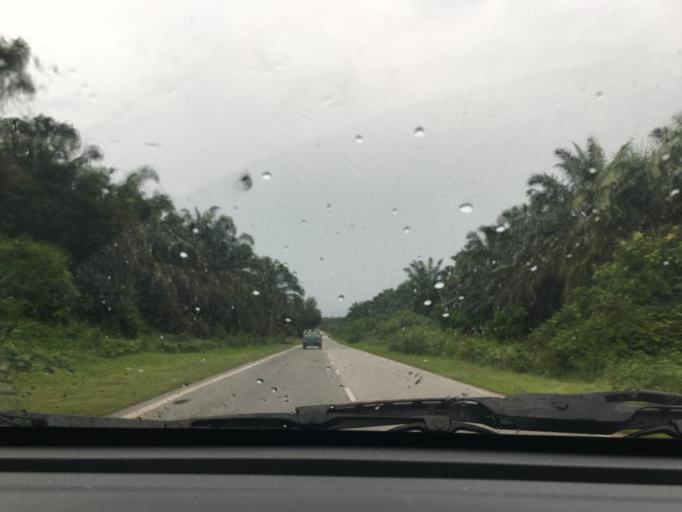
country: MY
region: Kedah
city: Sungai Petani
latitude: 5.6356
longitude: 100.6296
